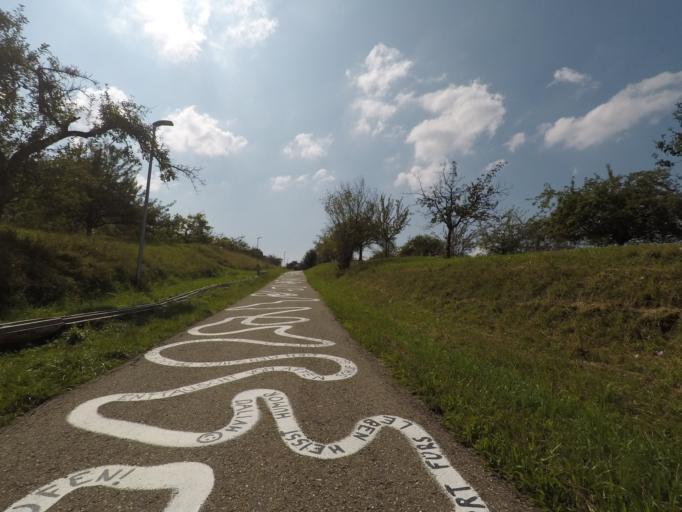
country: DE
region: Baden-Wuerttemberg
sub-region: Regierungsbezirk Stuttgart
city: Winterbach
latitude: 48.7948
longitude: 9.4719
